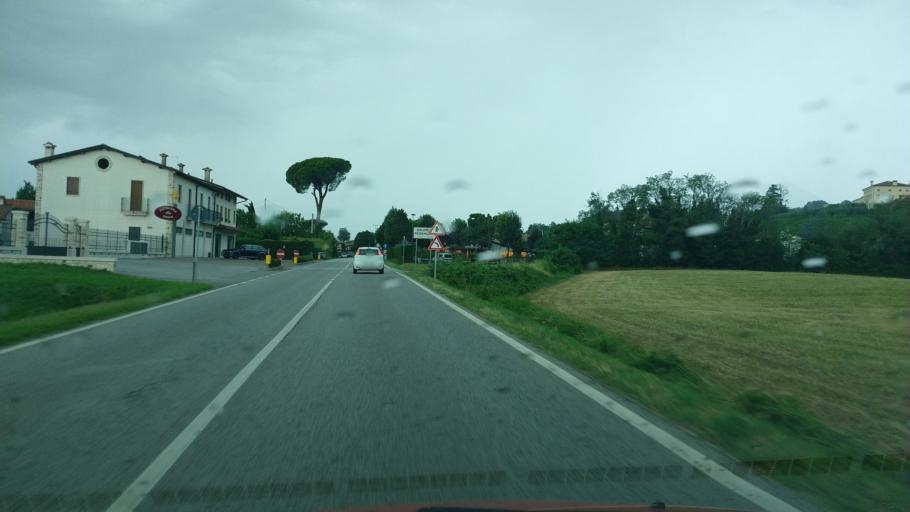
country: IT
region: Veneto
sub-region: Provincia di Vicenza
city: Grumolo Pedemonte
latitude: 45.7294
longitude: 11.5023
